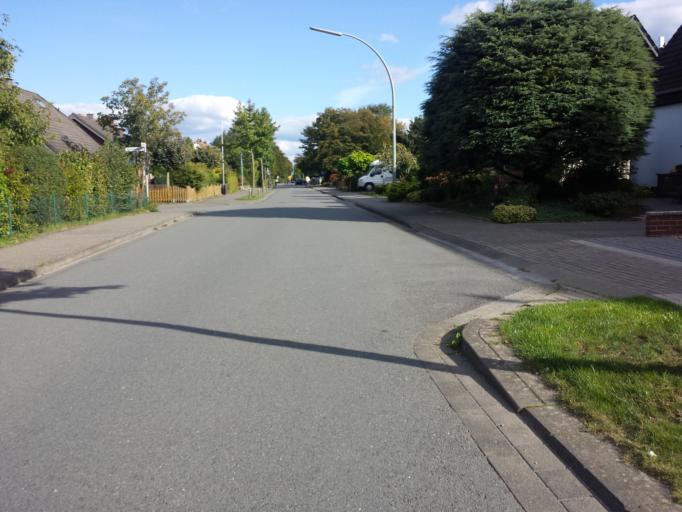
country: DE
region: North Rhine-Westphalia
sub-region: Regierungsbezirk Detmold
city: Langenberg
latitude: 51.7507
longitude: 8.3215
